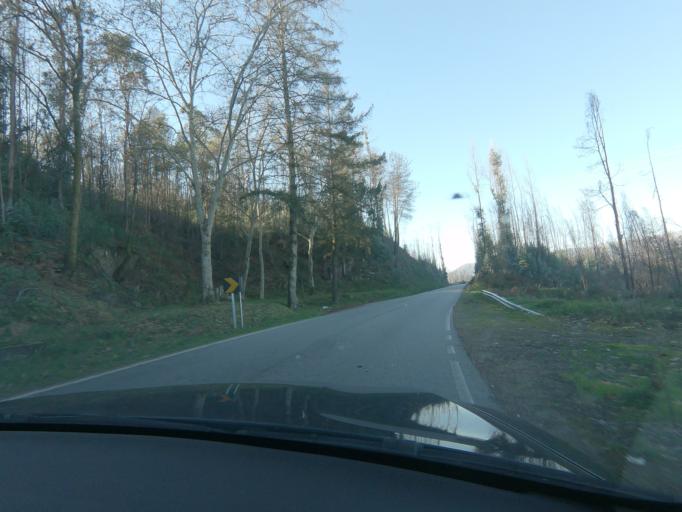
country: PT
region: Viseu
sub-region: Vouzela
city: Vouzela
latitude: 40.7273
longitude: -8.1340
